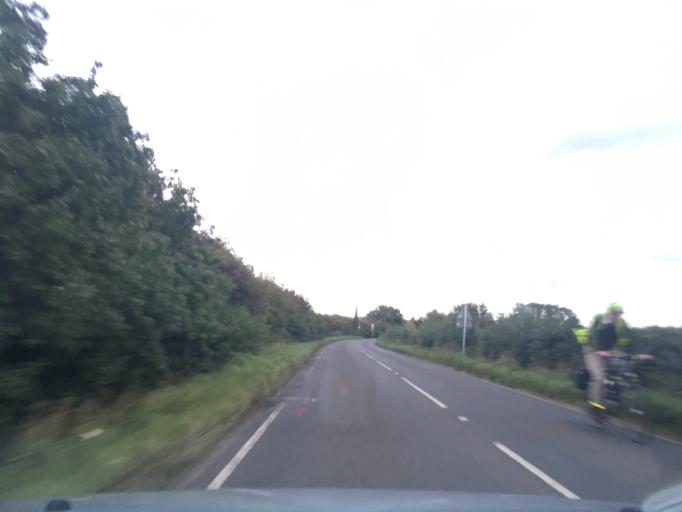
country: GB
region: England
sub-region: Oxfordshire
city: Kidlington
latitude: 51.8275
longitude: -1.2418
